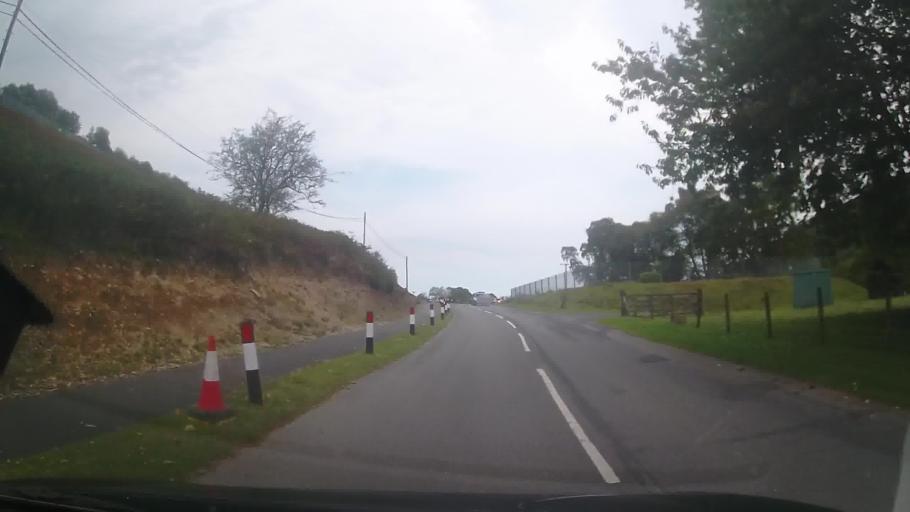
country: GB
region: Wales
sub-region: Sir Powys
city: Rhayader
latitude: 52.2744
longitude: -3.5662
